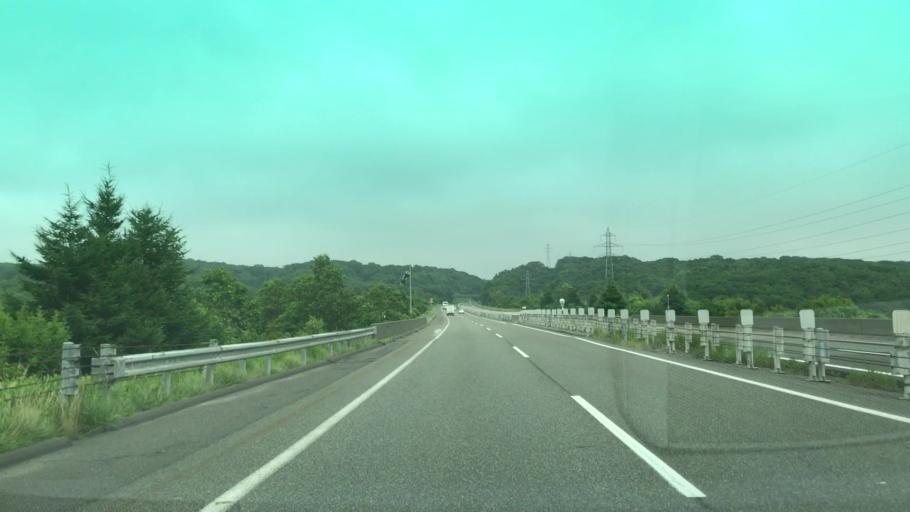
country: JP
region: Hokkaido
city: Tomakomai
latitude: 42.6571
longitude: 141.5739
